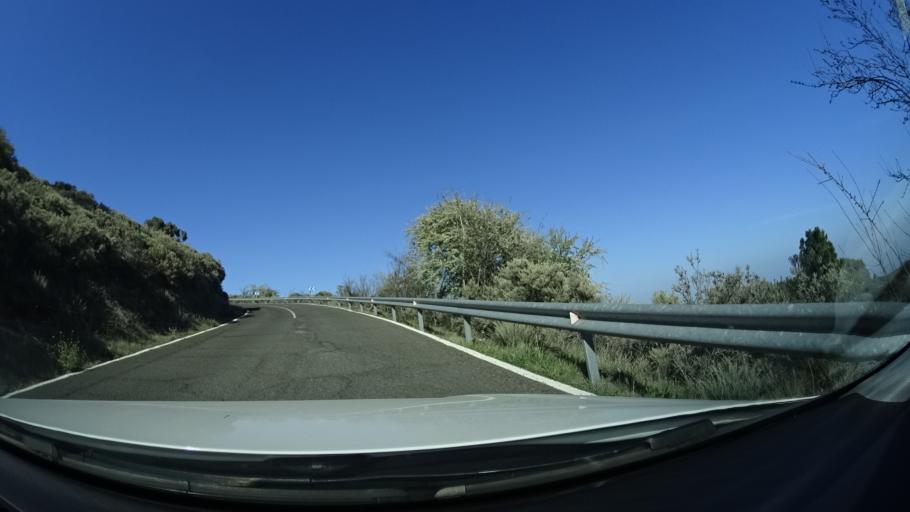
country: ES
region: Canary Islands
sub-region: Provincia de Las Palmas
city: San Bartolome
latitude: 27.9631
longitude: -15.5476
